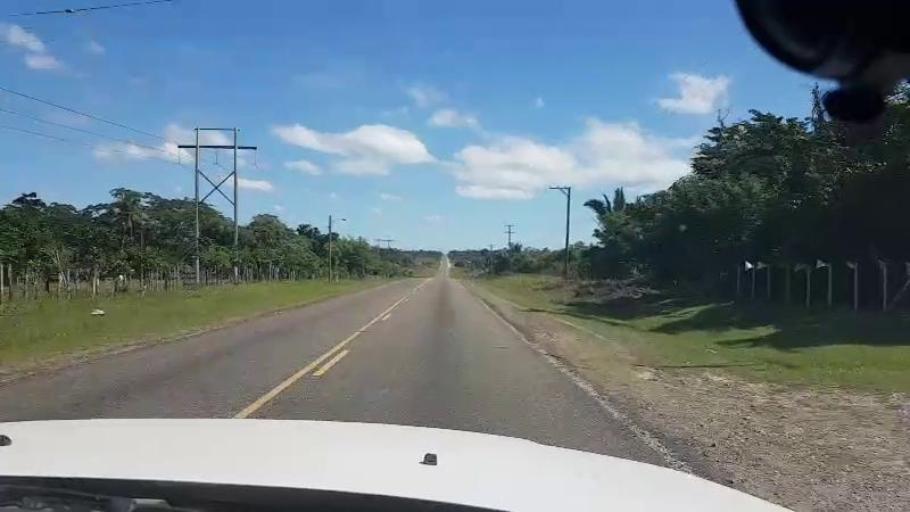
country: BZ
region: Cayo
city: Belmopan
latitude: 17.2768
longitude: -88.7279
